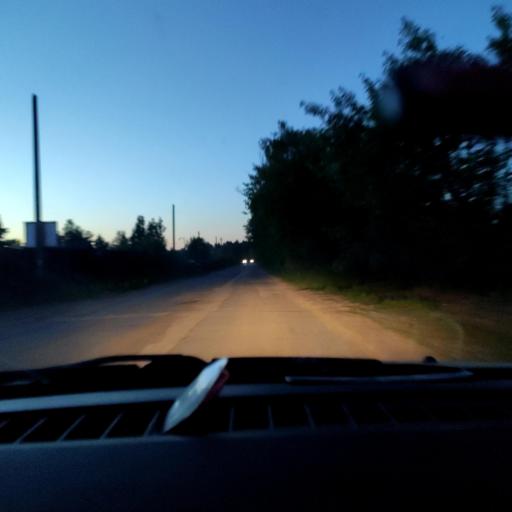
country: RU
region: Perm
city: Kultayevo
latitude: 57.9558
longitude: 55.9074
